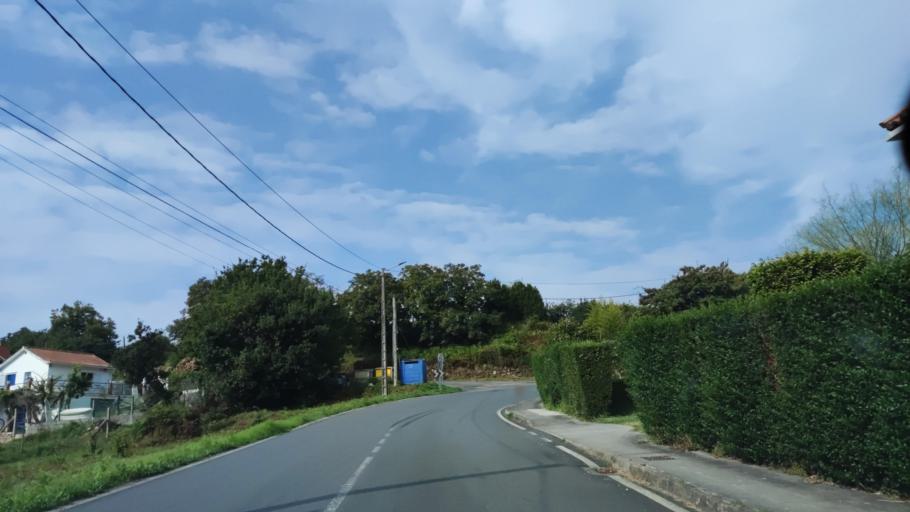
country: ES
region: Galicia
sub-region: Provincia da Coruna
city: Rianxo
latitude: 42.6476
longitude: -8.8051
